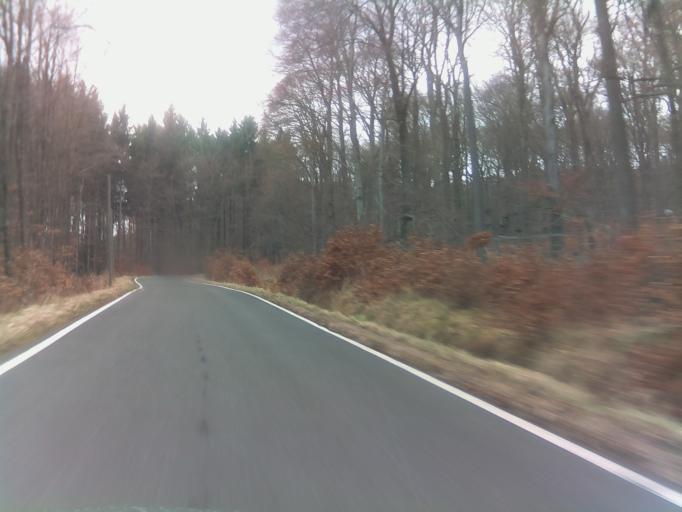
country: DE
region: Rheinland-Pfalz
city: Oberheimbach
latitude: 49.9919
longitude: 7.7697
